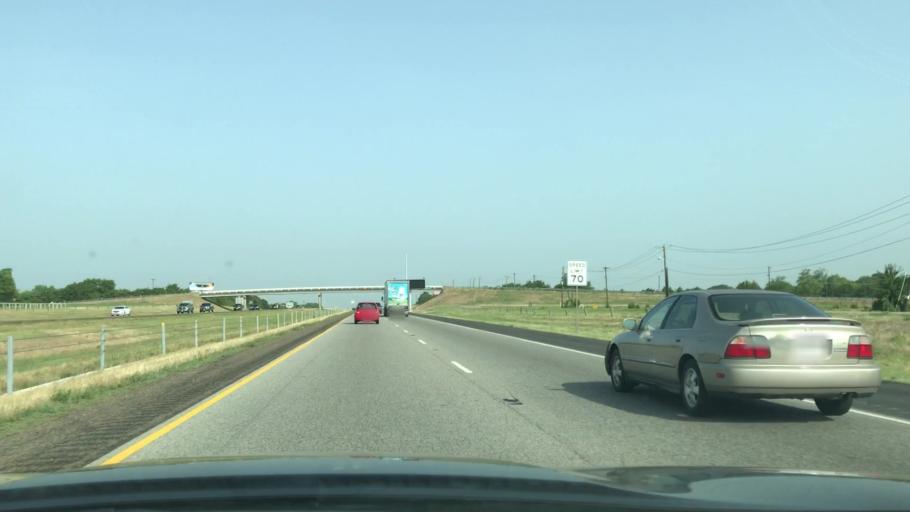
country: US
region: Texas
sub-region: Kaufman County
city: Terrell
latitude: 32.7060
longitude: -96.2855
